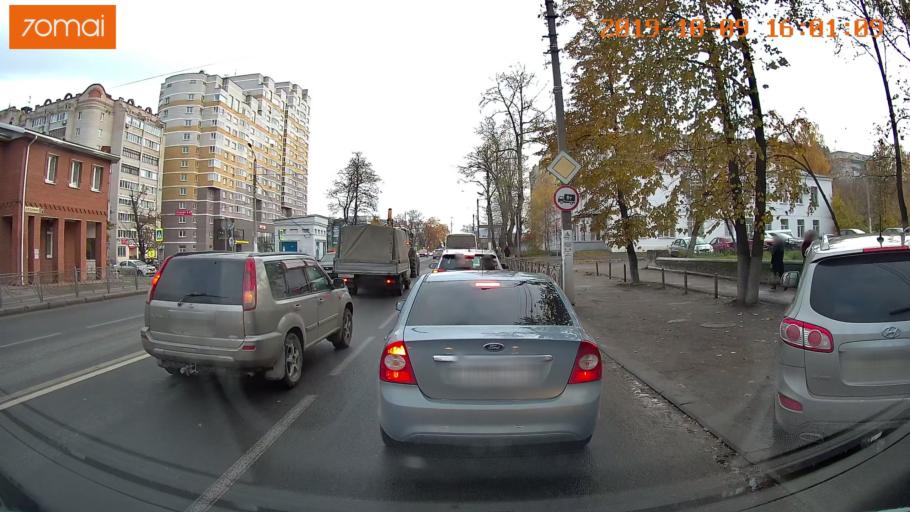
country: RU
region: Kostroma
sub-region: Kostromskoy Rayon
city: Kostroma
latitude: 57.7653
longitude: 40.9512
